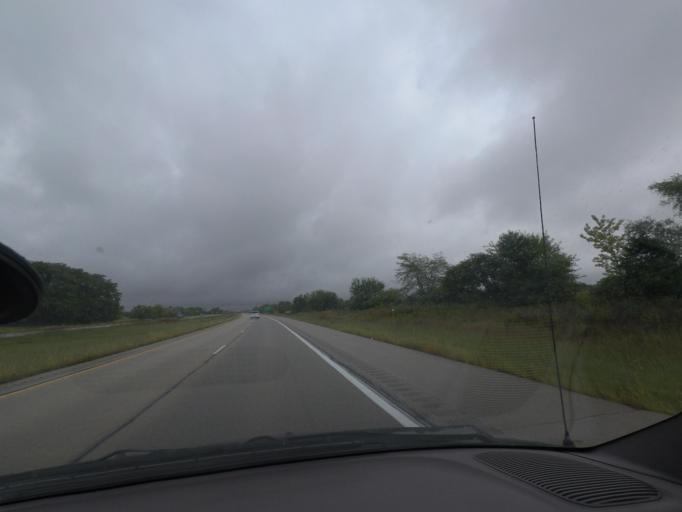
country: US
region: Illinois
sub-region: Piatt County
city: Monticello
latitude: 40.0767
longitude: -88.5317
